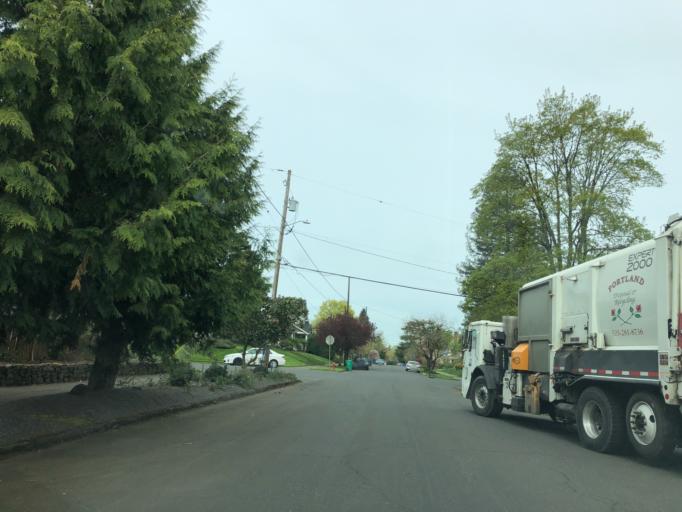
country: US
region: Oregon
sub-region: Multnomah County
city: Portland
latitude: 45.5517
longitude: -122.6354
